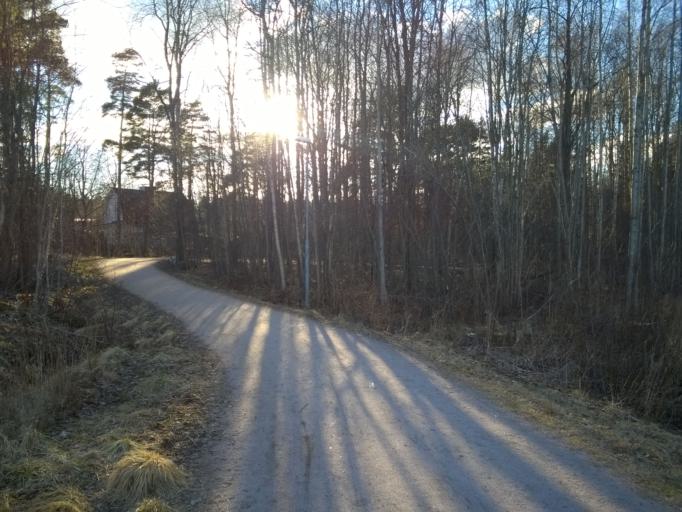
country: FI
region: Uusimaa
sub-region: Helsinki
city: Vantaa
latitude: 60.2469
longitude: 25.0391
